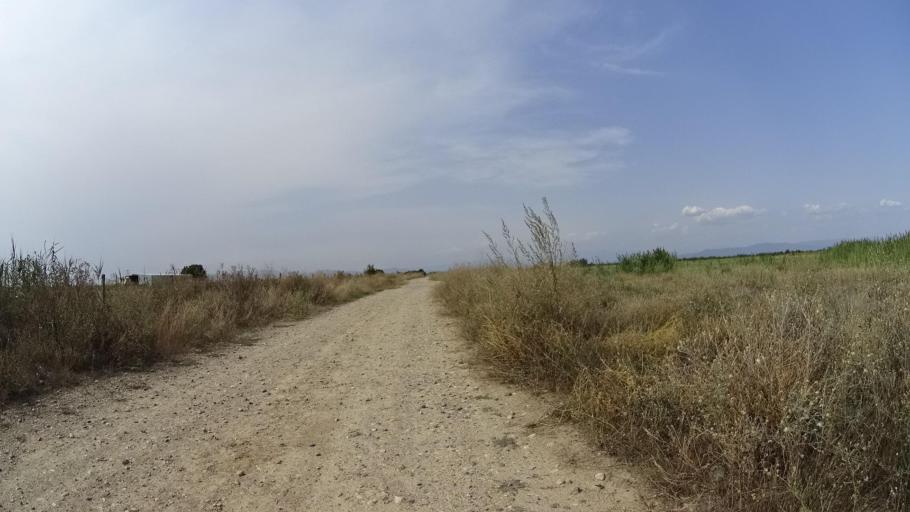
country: BG
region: Plovdiv
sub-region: Obshtina Kaloyanovo
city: Kaloyanovo
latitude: 42.2848
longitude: 24.7978
